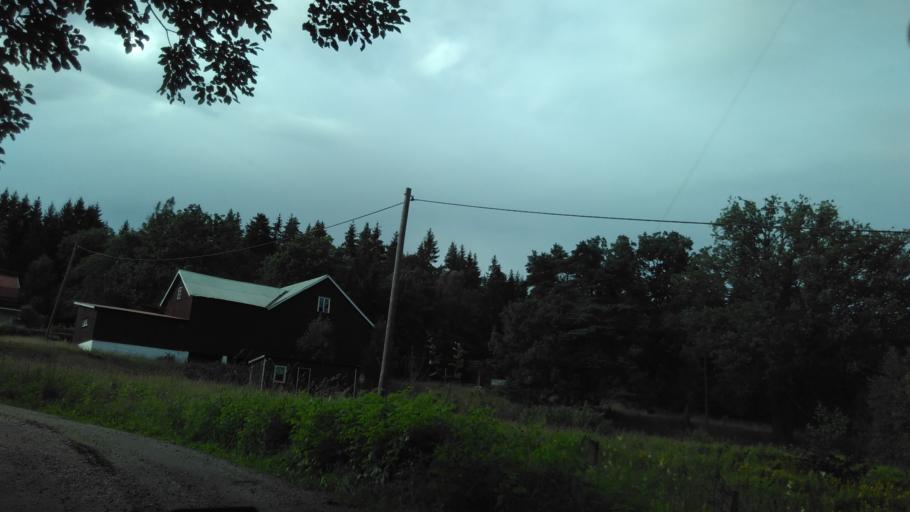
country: SE
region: Vaestra Goetaland
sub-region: Alingsas Kommun
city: Alingsas
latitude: 57.9932
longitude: 12.6006
